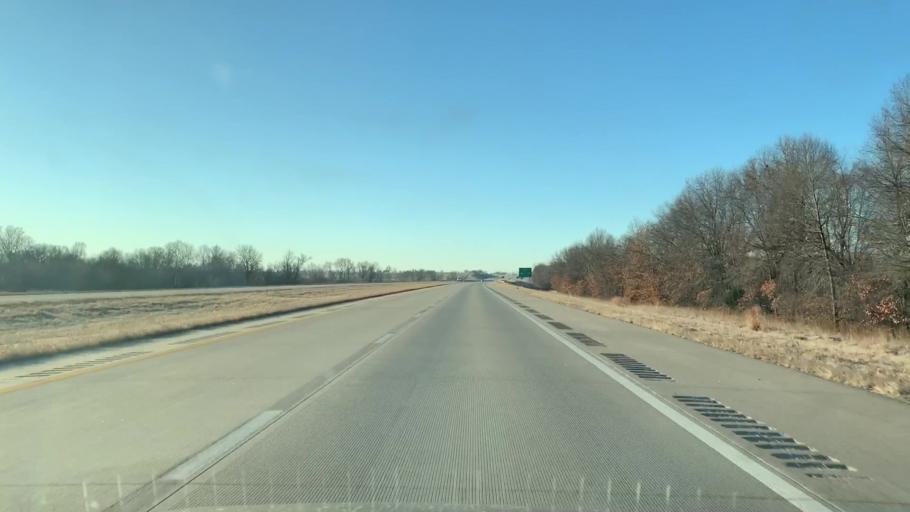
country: US
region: Kansas
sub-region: Linn County
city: Pleasanton
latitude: 38.0145
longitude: -94.7039
